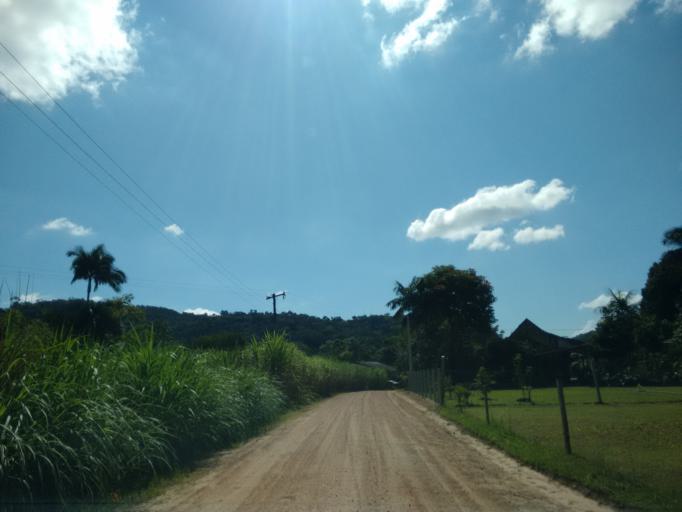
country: BR
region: Santa Catarina
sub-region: Indaial
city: Indaial
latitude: -26.9468
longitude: -49.1801
